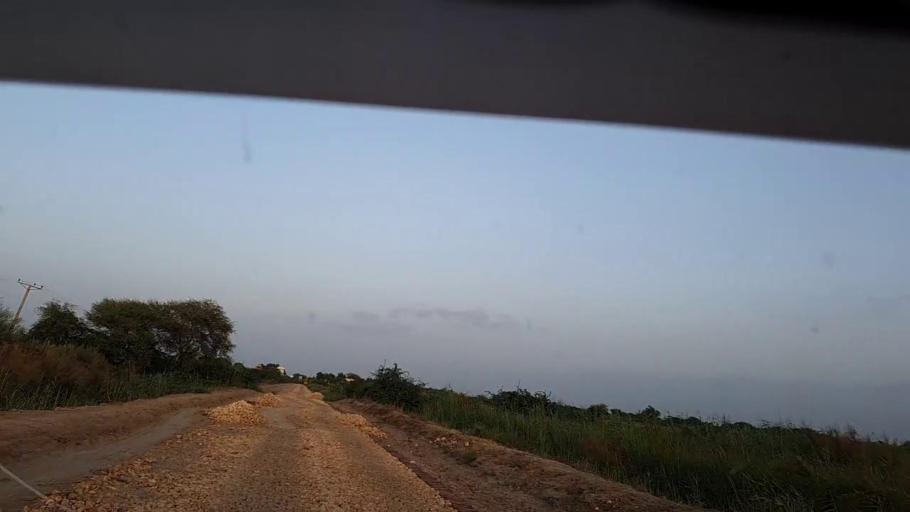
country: PK
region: Sindh
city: Kadhan
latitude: 24.5293
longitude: 68.9530
